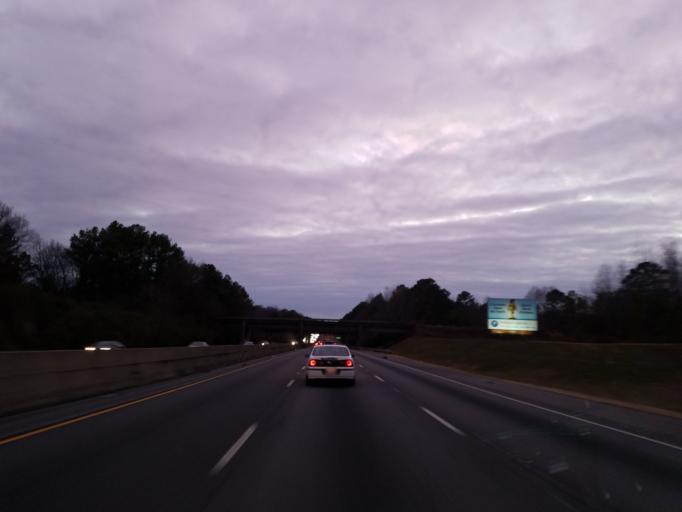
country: US
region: Alabama
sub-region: Jefferson County
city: Leeds
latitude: 33.5565
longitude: -86.5701
